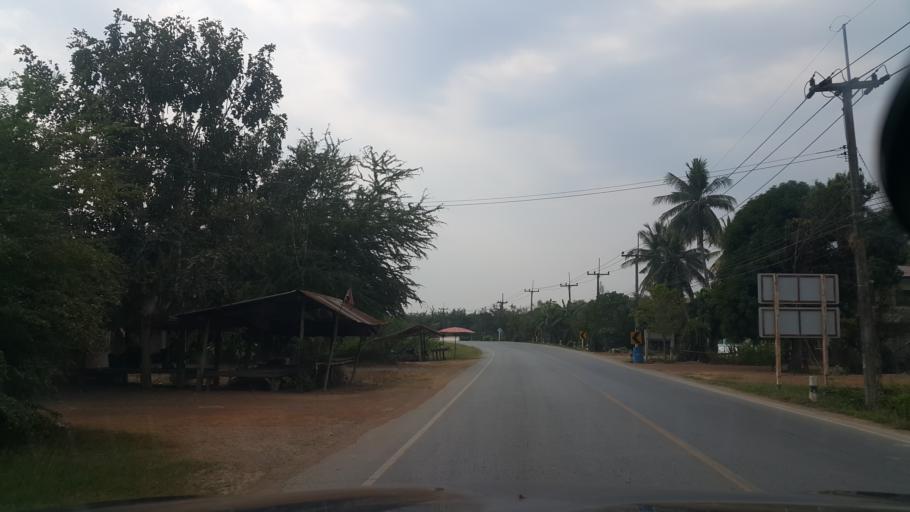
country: TH
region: Sukhothai
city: Si Samrong
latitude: 17.0820
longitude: 99.8810
